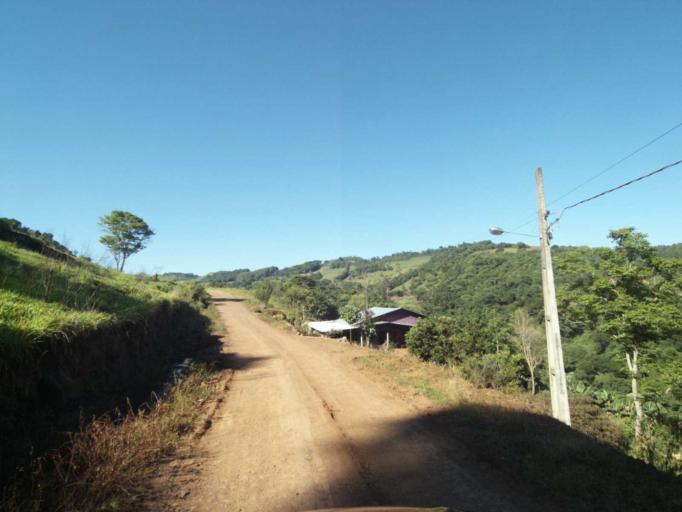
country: BR
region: Parana
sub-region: Francisco Beltrao
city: Francisco Beltrao
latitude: -26.1462
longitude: -53.3121
